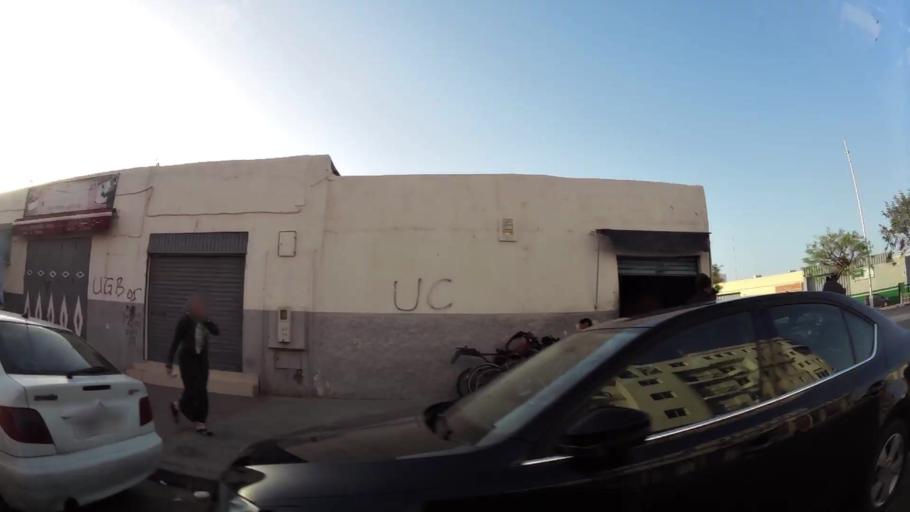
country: MA
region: Oued ed Dahab-Lagouira
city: Dakhla
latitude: 30.4167
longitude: -9.5743
